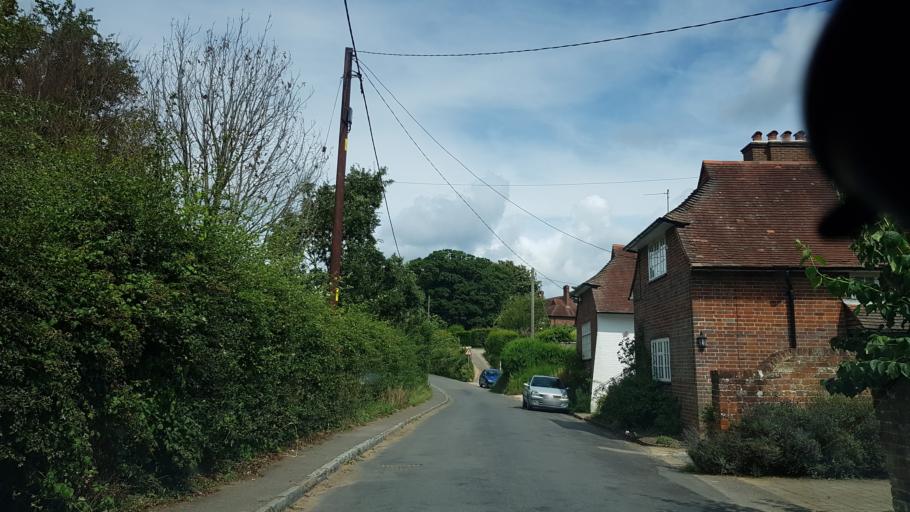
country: GB
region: England
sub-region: Surrey
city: Elstead
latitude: 51.1473
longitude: -0.7120
